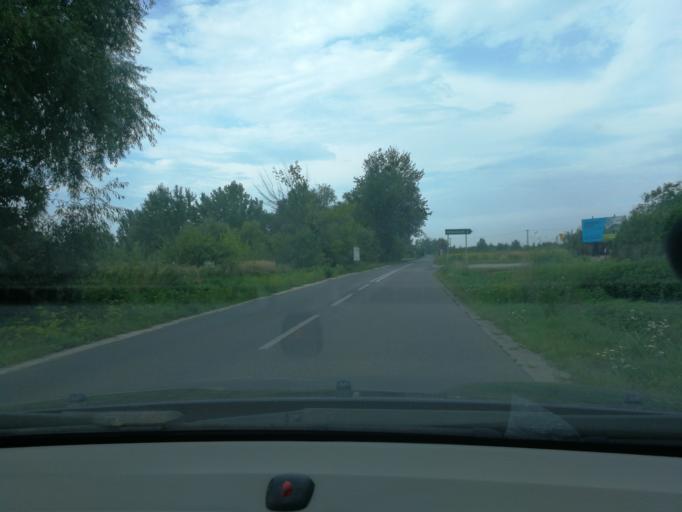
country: PL
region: Masovian Voivodeship
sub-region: Powiat grodziski
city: Grodzisk Mazowiecki
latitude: 52.1420
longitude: 20.6315
